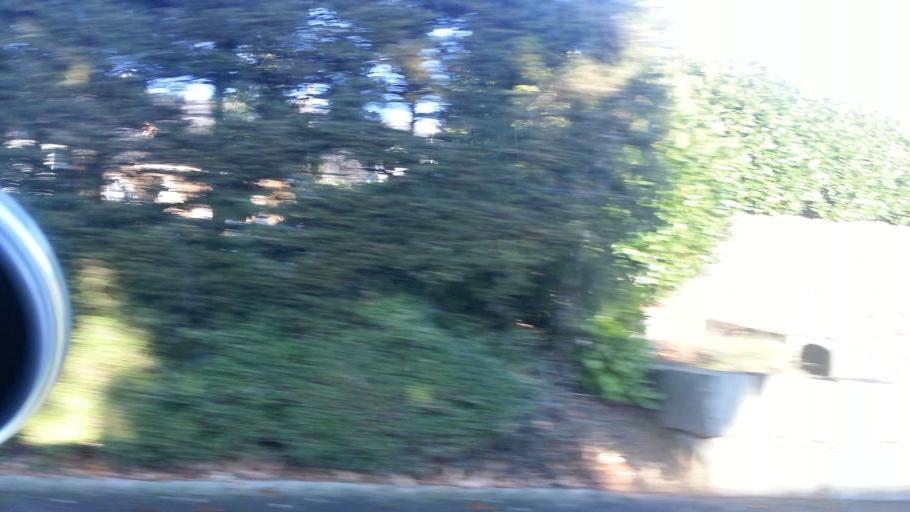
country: DE
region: Saarland
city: Tholey
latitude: 49.4768
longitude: 7.0286
